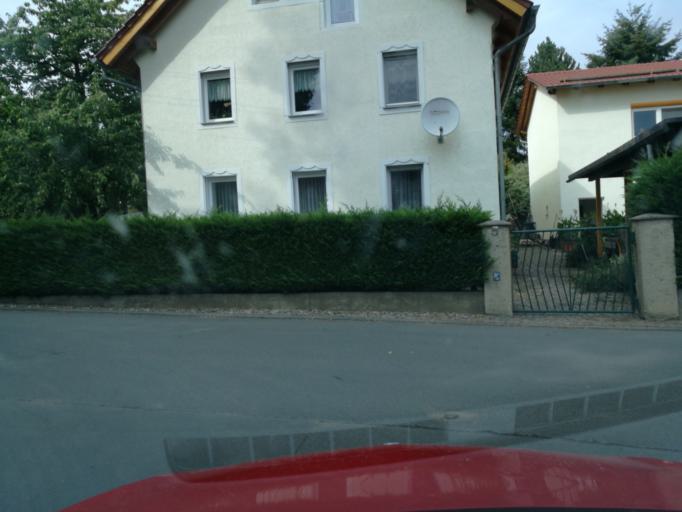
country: DE
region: Saxony
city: Oschatz
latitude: 51.2820
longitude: 13.0825
